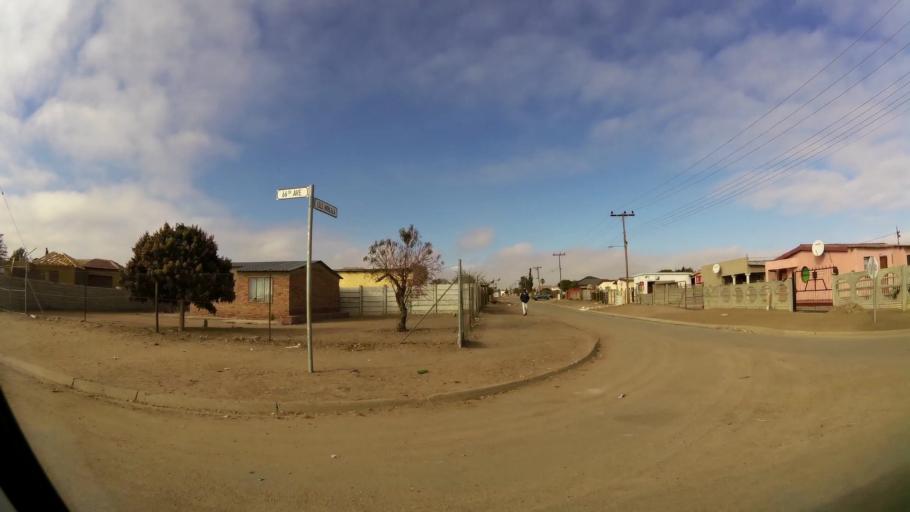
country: ZA
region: Limpopo
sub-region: Capricorn District Municipality
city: Polokwane
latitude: -23.8420
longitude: 29.3826
